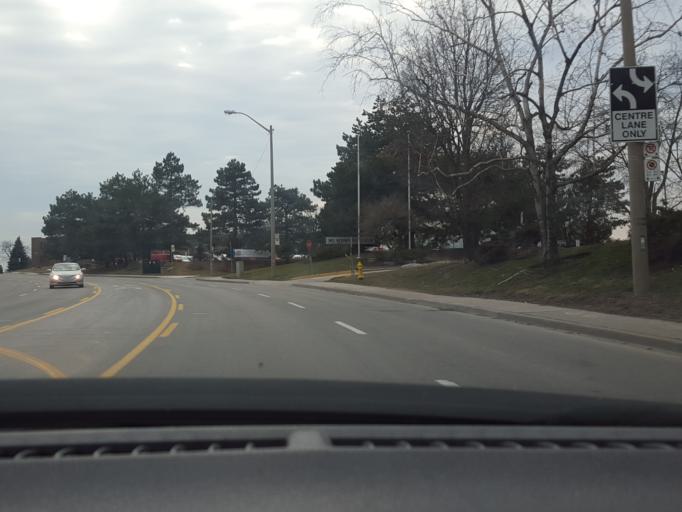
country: CA
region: Ontario
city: Willowdale
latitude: 43.7262
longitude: -79.3327
